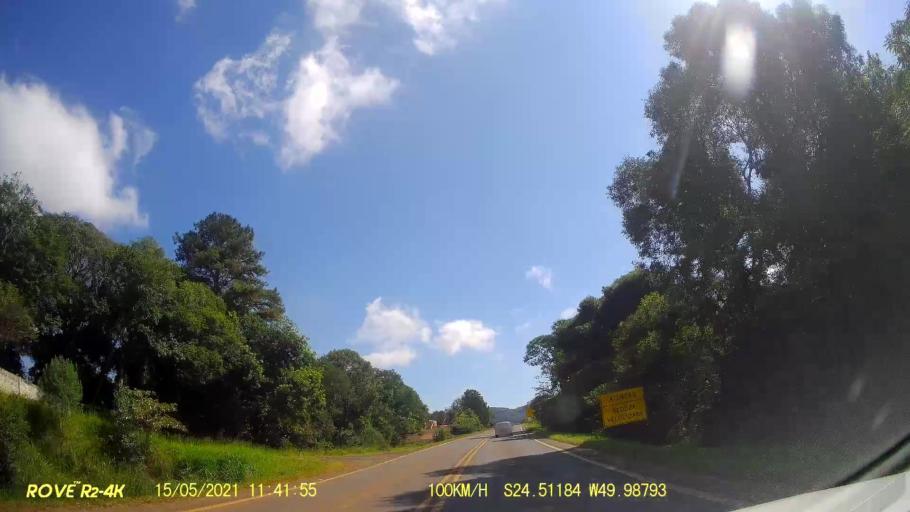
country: BR
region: Parana
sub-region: Pirai Do Sul
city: Pirai do Sul
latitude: -24.5118
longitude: -49.9878
